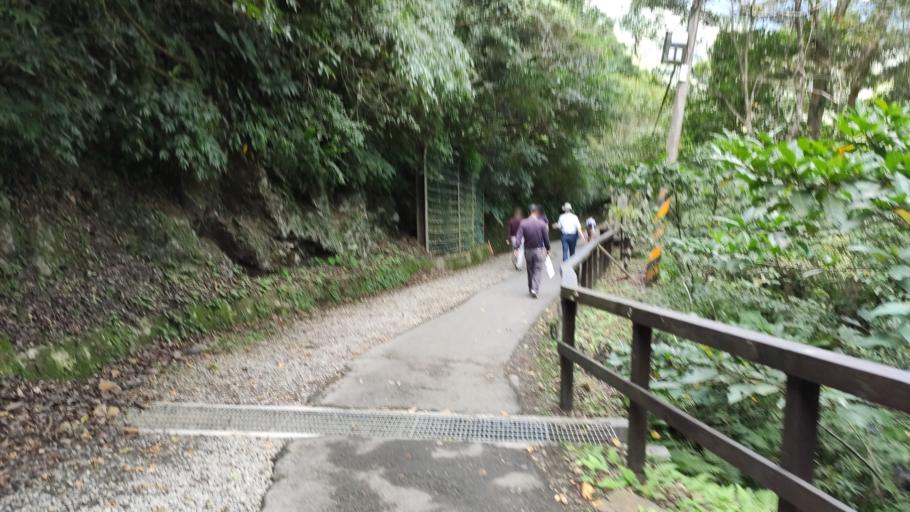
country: TW
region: Taiwan
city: Daxi
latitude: 24.8271
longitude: 121.4472
